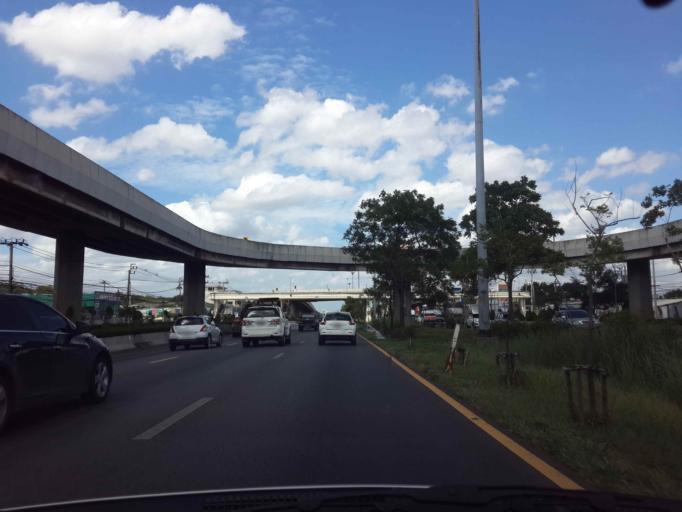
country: TH
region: Bangkok
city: Bang Bon
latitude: 13.6134
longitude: 100.3807
